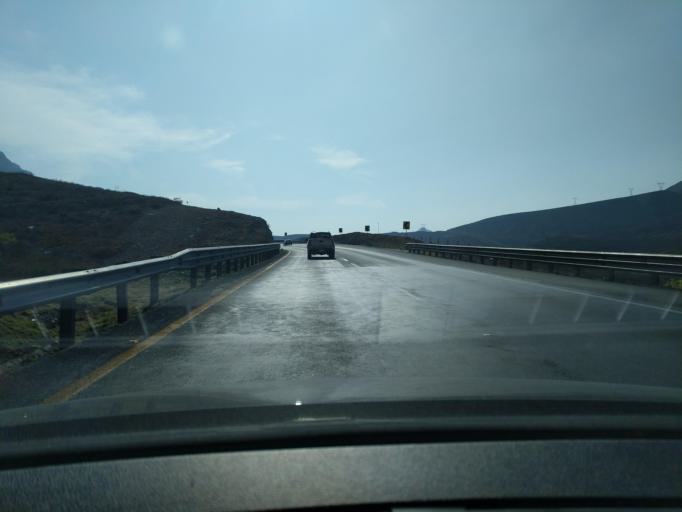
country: MX
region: Nuevo Leon
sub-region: Garcia
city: Las Torres de Guadalupe
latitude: 25.6531
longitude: -100.7263
